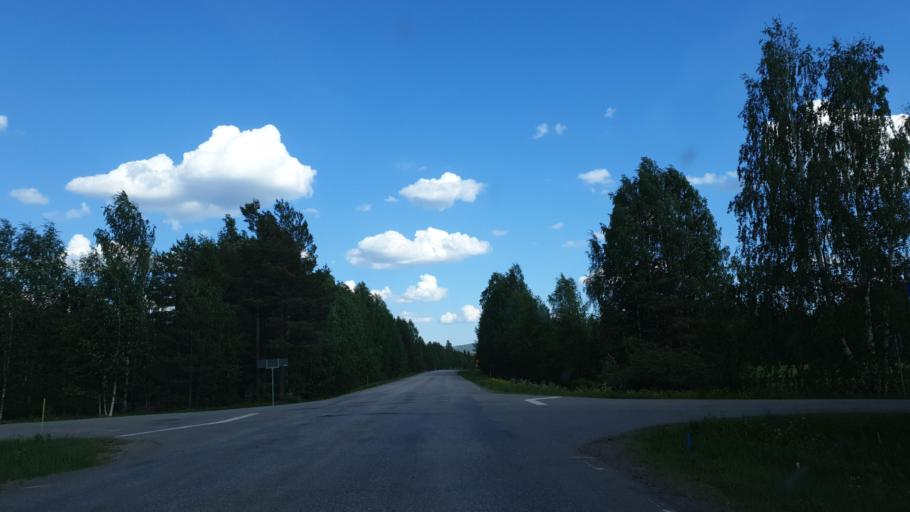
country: SE
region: Norrbotten
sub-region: Alvsbyns Kommun
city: AElvsbyn
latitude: 65.8454
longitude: 20.4814
